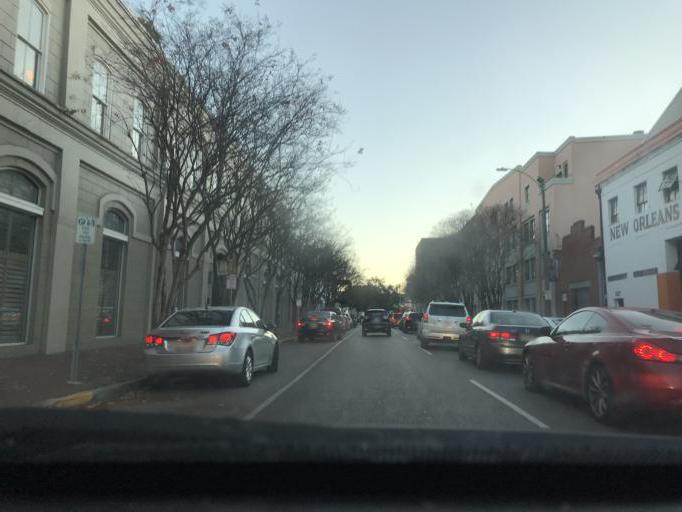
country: US
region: Louisiana
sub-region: Orleans Parish
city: New Orleans
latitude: 29.9445
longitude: -90.0675
